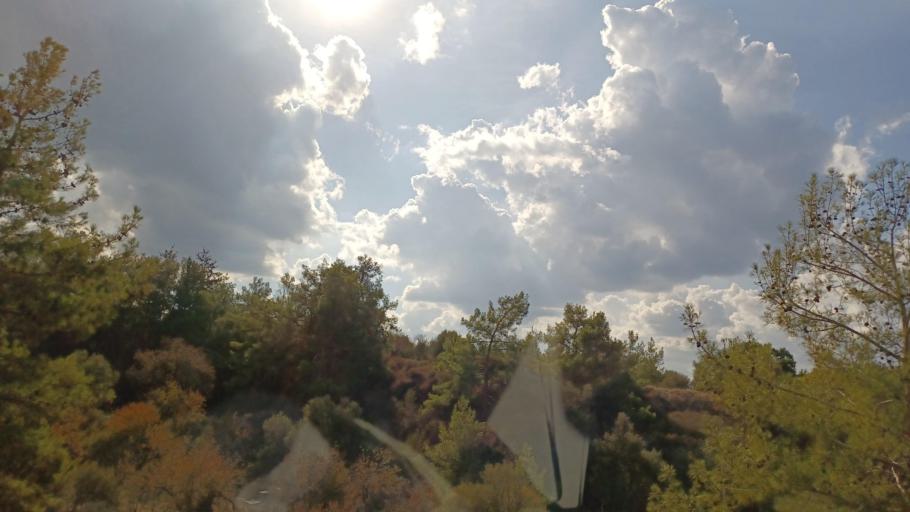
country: CY
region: Pafos
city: Polis
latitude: 35.1389
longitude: 32.5253
